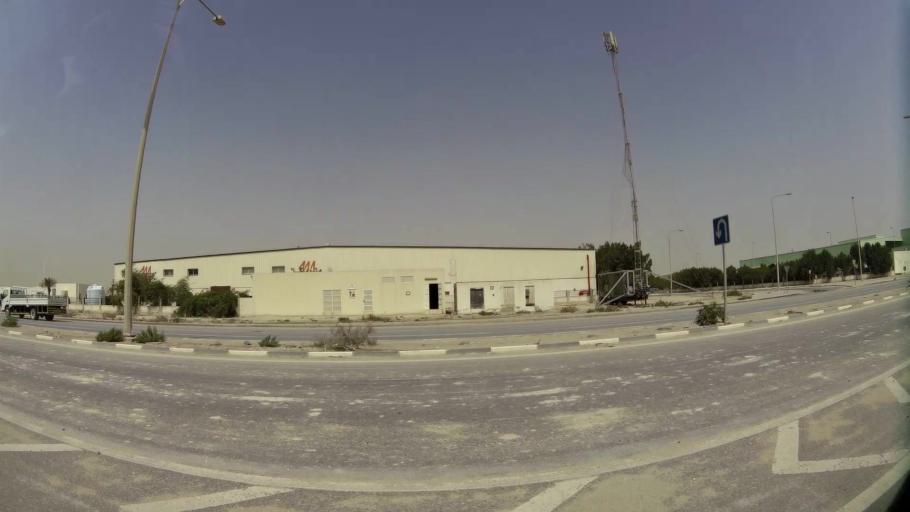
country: QA
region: Al Wakrah
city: Al Wukayr
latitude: 25.1636
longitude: 51.4157
